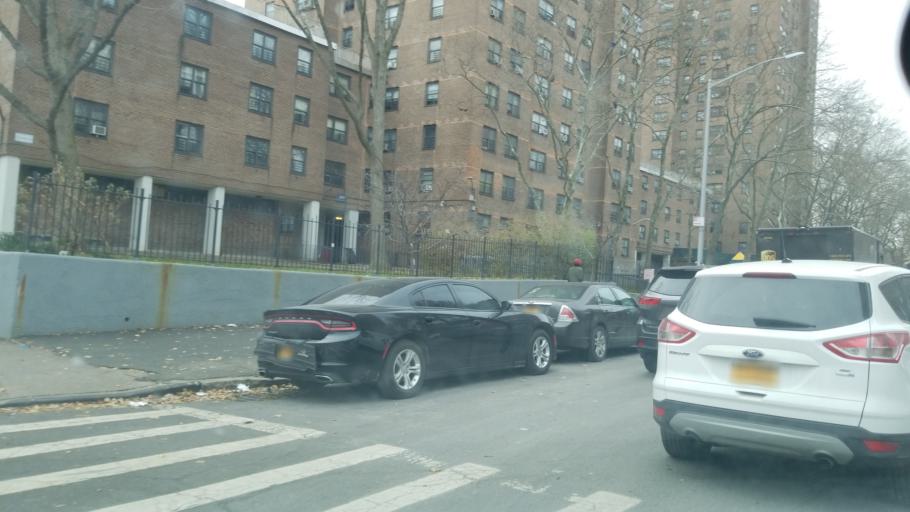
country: US
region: New York
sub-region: New York County
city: Inwood
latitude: 40.8123
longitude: -73.9206
